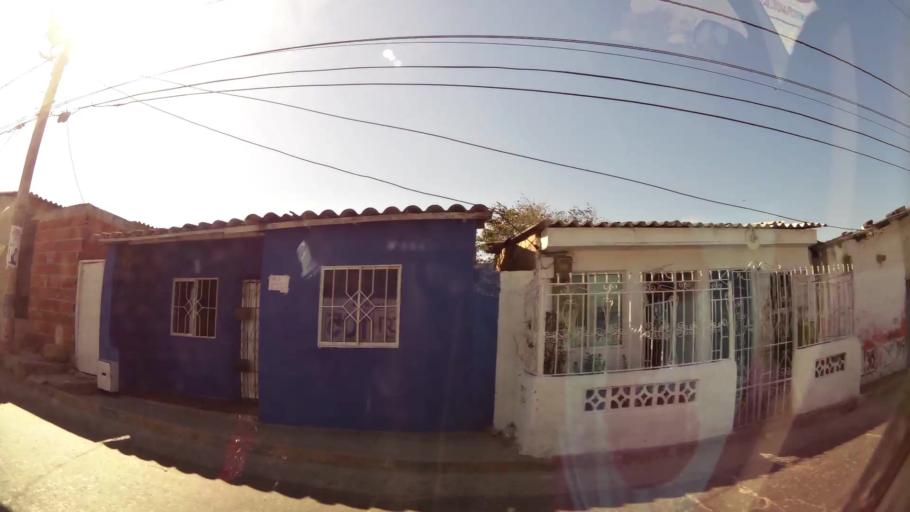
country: CO
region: Atlantico
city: Barranquilla
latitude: 10.9391
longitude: -74.8097
